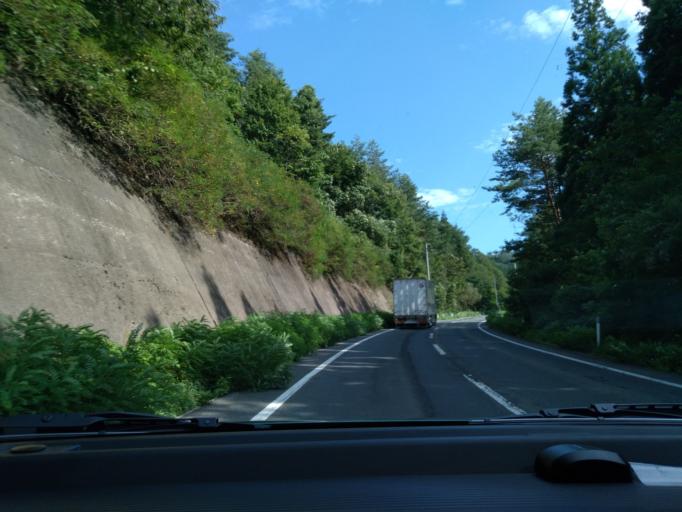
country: JP
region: Iwate
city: Shizukuishi
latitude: 39.6398
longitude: 141.0153
